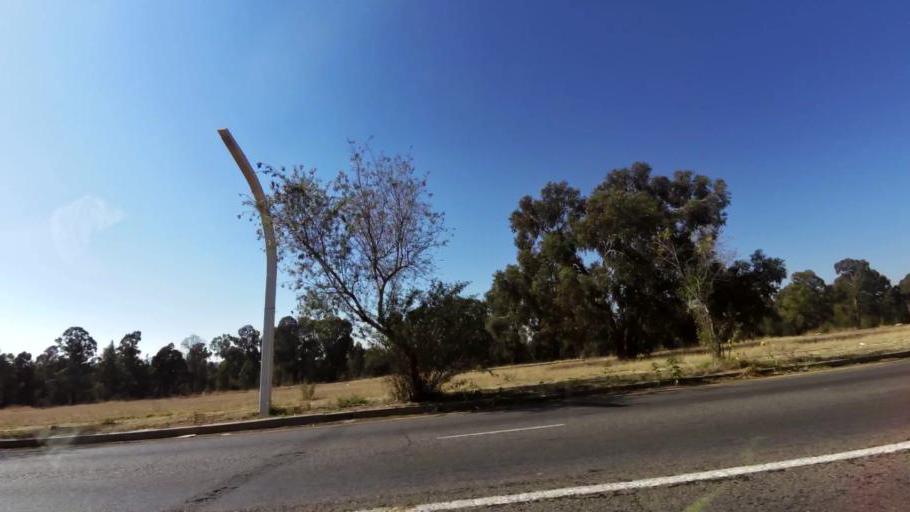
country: ZA
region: Gauteng
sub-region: City of Johannesburg Metropolitan Municipality
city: Johannesburg
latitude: -26.2416
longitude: 27.9855
